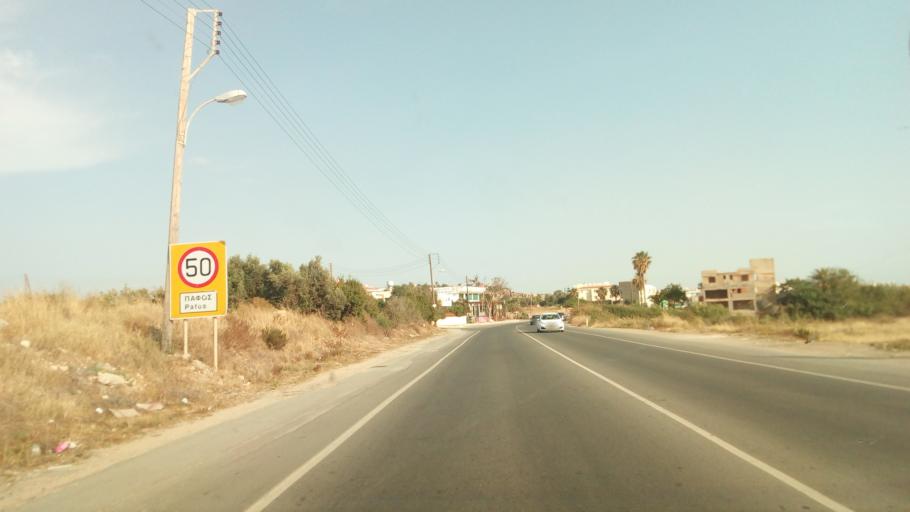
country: CY
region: Pafos
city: Chlorakas
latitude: 34.7877
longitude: 32.4043
